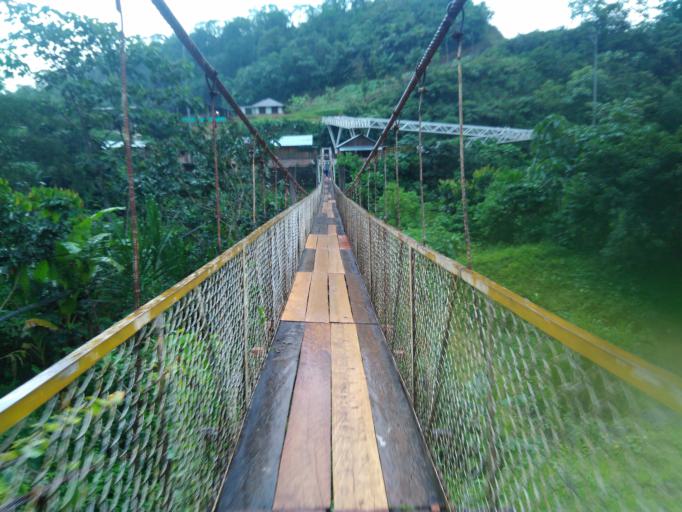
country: CO
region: Valle del Cauca
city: Buenaventura
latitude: 3.8569
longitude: -76.8505
